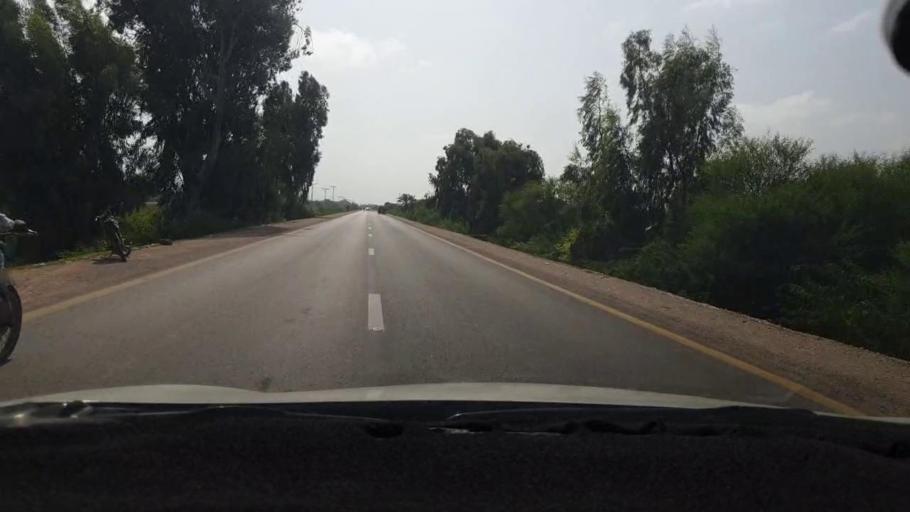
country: PK
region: Sindh
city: Mirpur Khas
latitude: 25.7355
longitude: 69.1006
